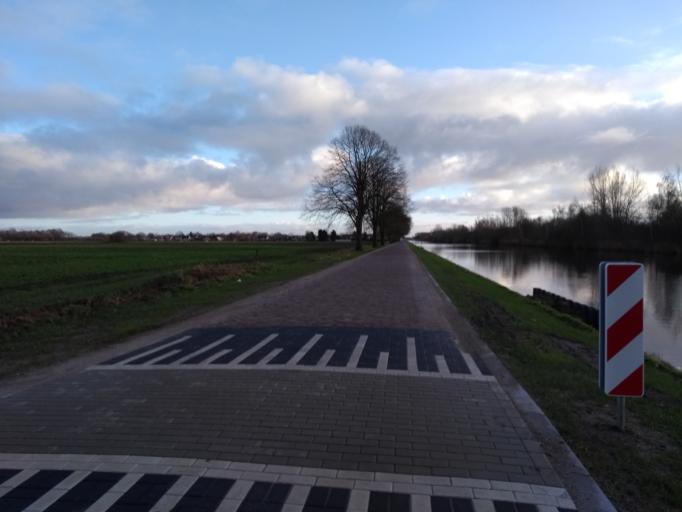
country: NL
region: Overijssel
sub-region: Gemeente Twenterand
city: Vriezenveen
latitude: 52.3860
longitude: 6.6159
